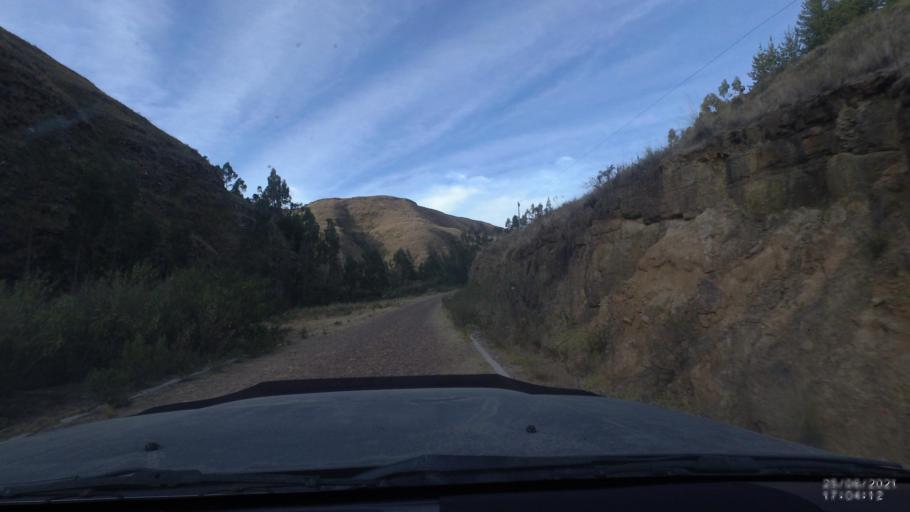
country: BO
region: Cochabamba
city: Arani
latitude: -17.8321
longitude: -65.7231
